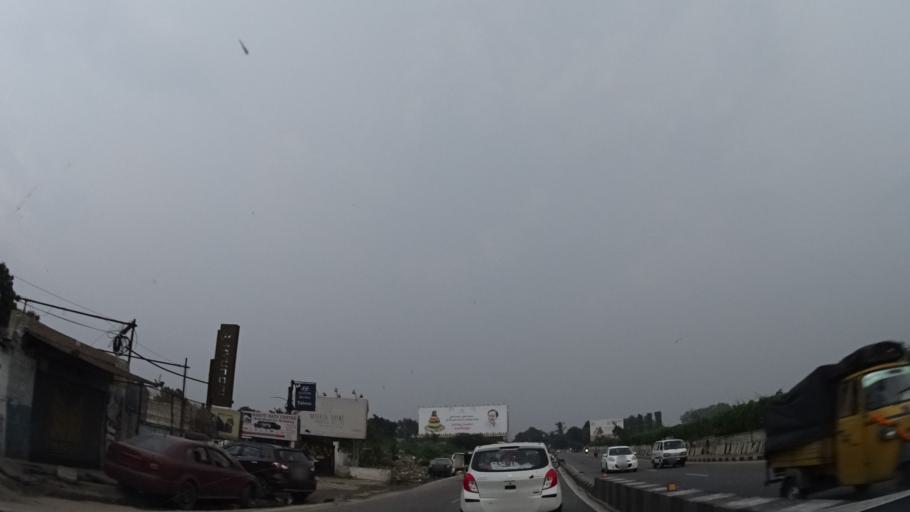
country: IN
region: Telangana
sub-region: Hyderabad
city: Malkajgiri
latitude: 17.4539
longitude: 78.4858
